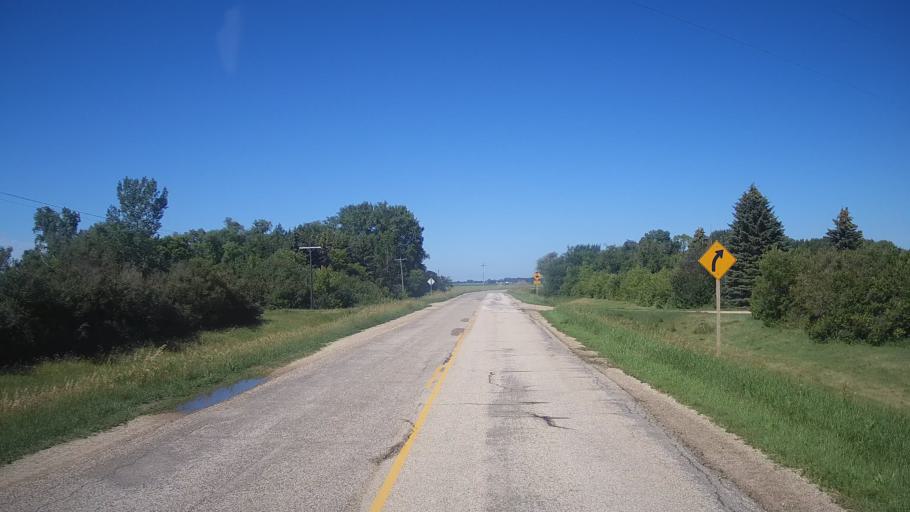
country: CA
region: Manitoba
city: Portage la Prairie
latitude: 50.0444
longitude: -98.0290
